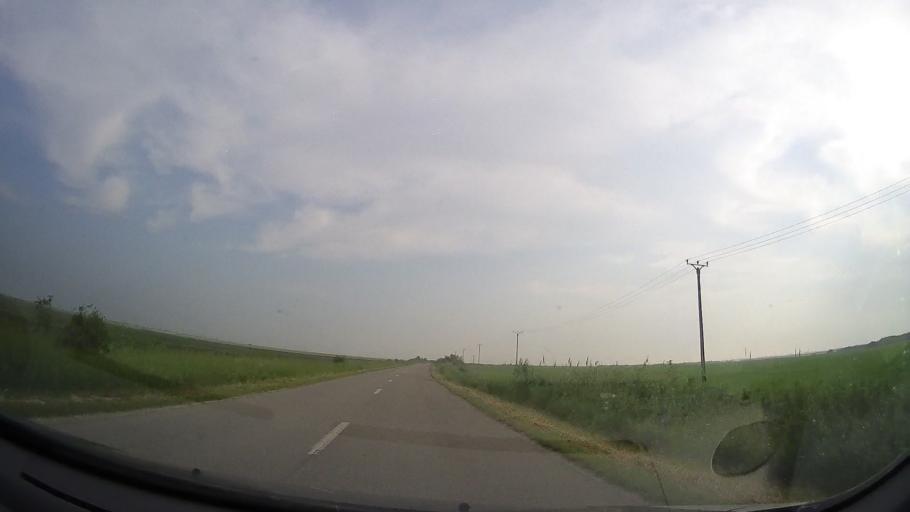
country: RO
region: Timis
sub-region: Comuna Giulvaz
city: Giulvaz
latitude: 45.5363
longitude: 20.9482
